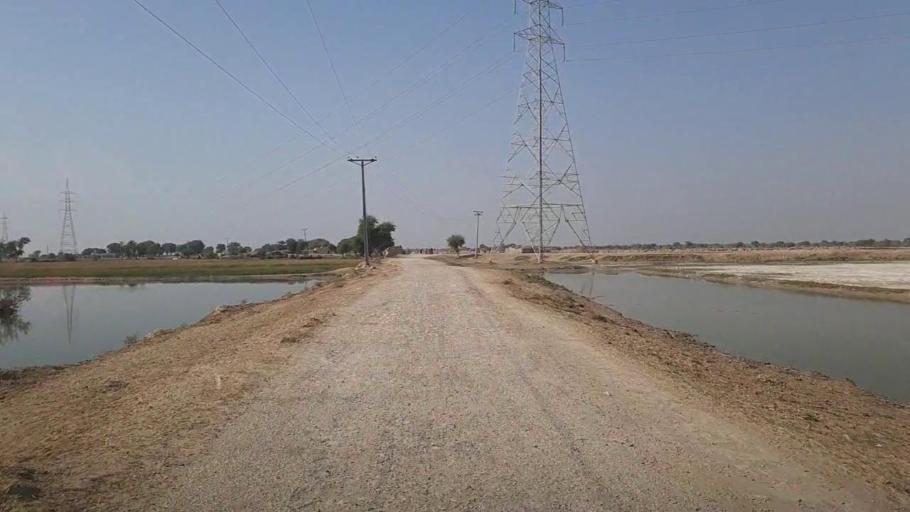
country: PK
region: Sindh
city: Kandhkot
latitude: 28.4112
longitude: 69.2441
